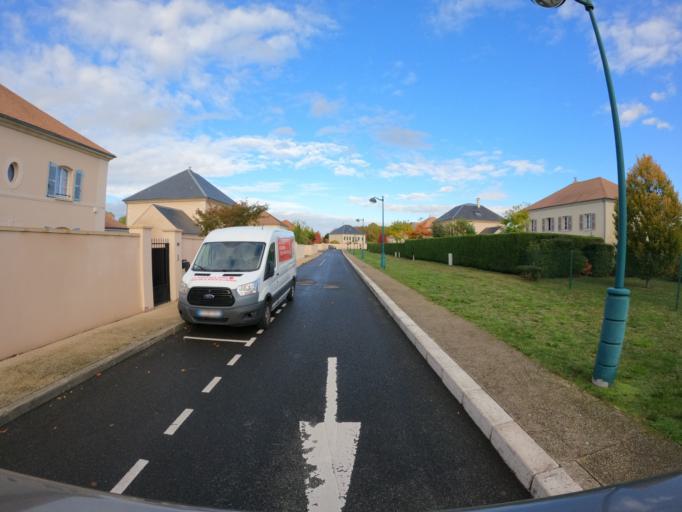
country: FR
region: Ile-de-France
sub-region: Departement de Seine-et-Marne
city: Bailly-Romainvilliers
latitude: 48.8530
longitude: 2.8228
